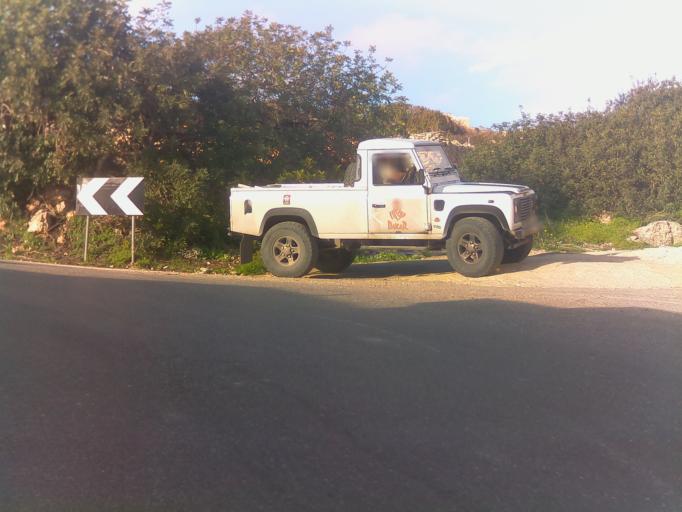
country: MT
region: Il-Mellieha
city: Mellieha
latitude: 35.9481
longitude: 14.3517
